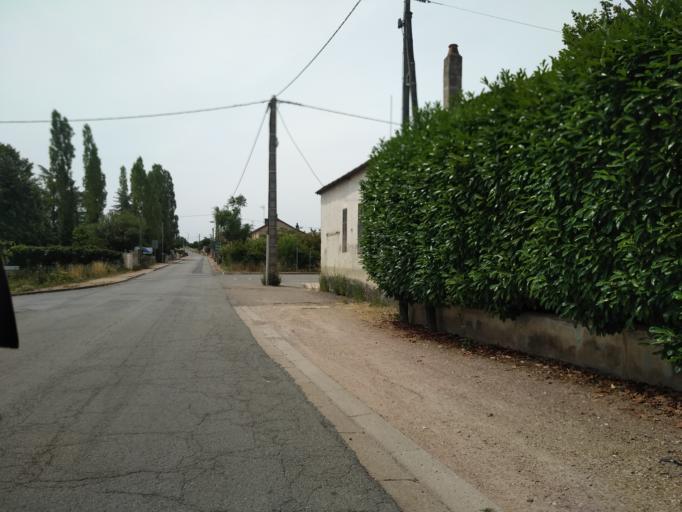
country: FR
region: Bourgogne
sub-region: Departement de Saone-et-Loire
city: Digoin
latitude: 46.4752
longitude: 3.9663
